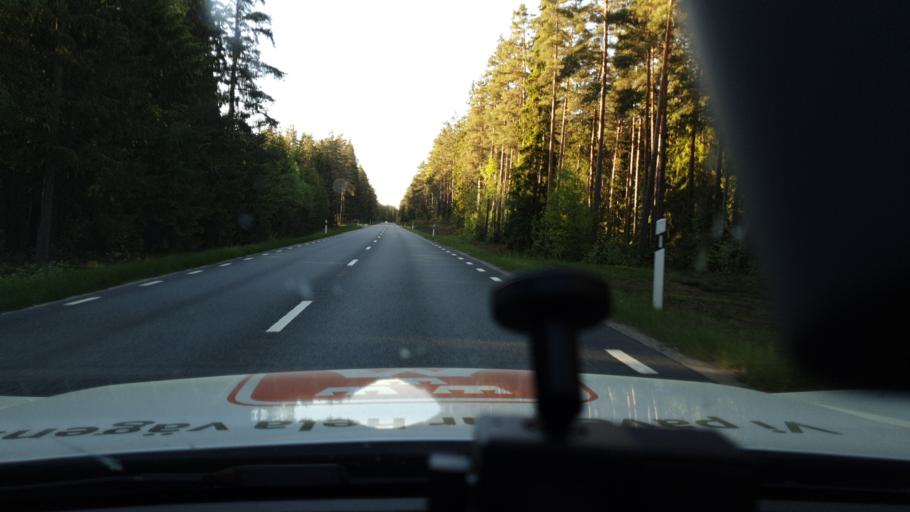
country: SE
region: Joenkoeping
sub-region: Vetlanda Kommun
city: Ekenassjon
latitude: 57.5799
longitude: 14.9712
